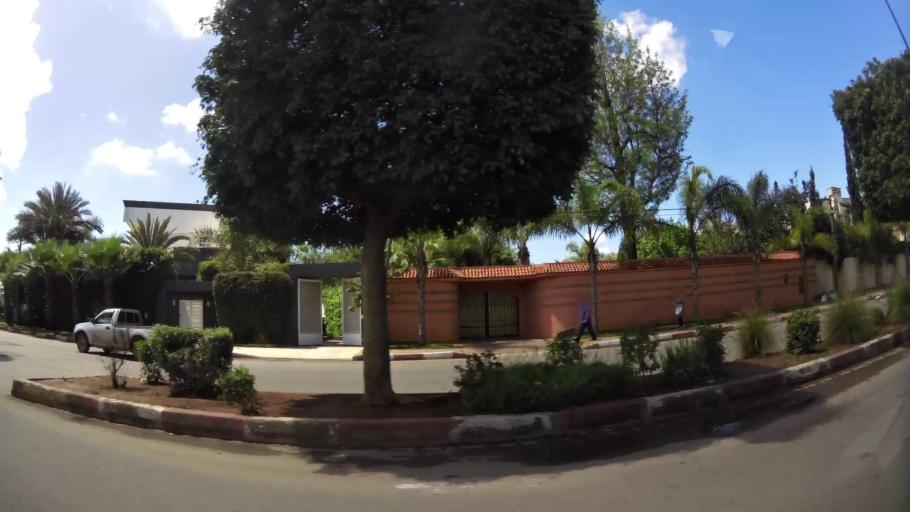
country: MA
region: Grand Casablanca
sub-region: Casablanca
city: Casablanca
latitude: 33.5223
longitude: -7.6319
